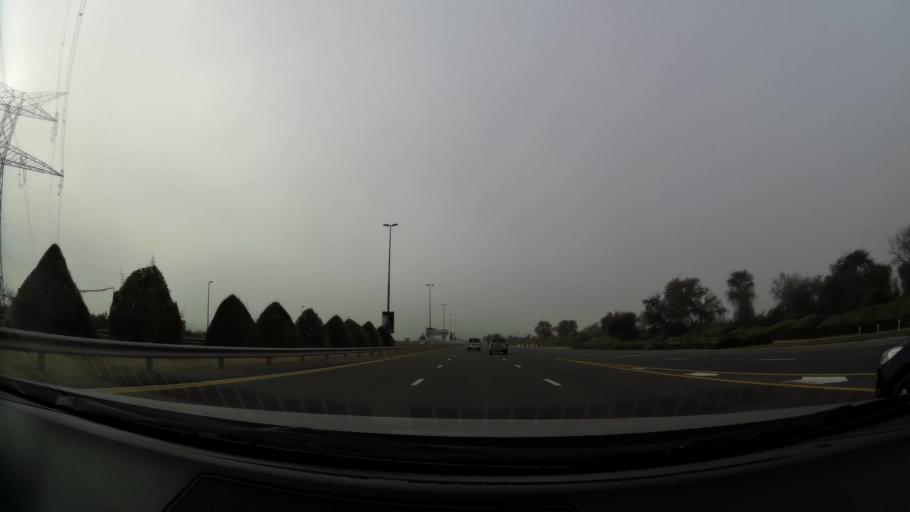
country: AE
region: Dubai
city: Dubai
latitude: 25.1677
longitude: 55.3263
